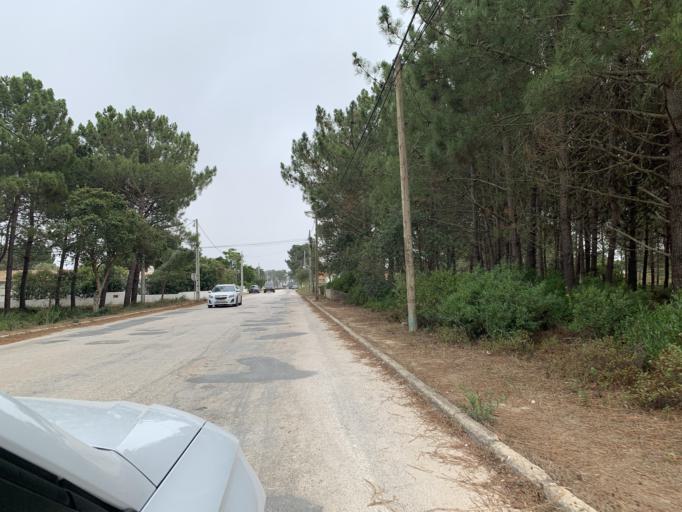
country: PT
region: Faro
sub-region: Aljezur
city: Aljezur
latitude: 37.3082
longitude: -8.8526
